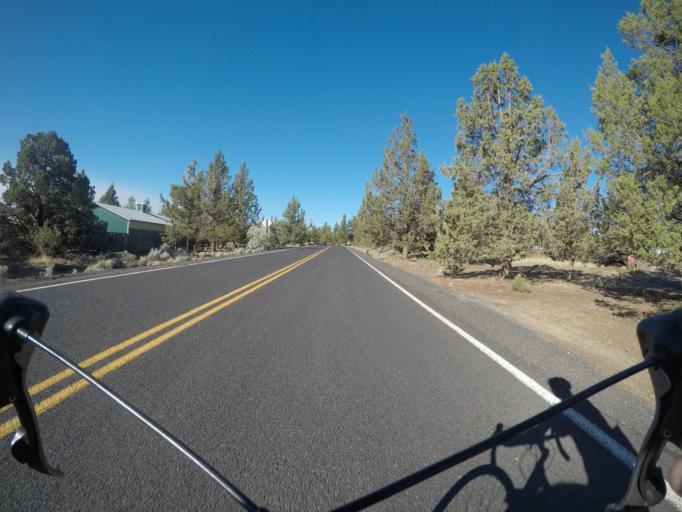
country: US
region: Oregon
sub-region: Deschutes County
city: Bend
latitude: 44.1753
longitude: -121.2653
